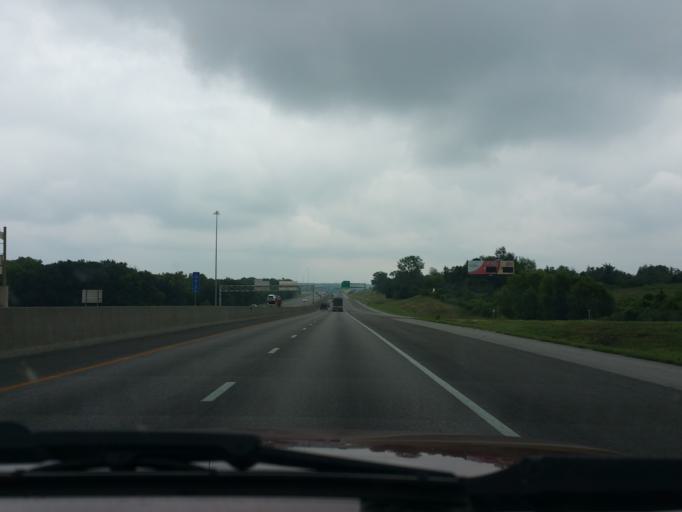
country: US
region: Kansas
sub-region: Wyandotte County
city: Edwardsville
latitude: 39.1060
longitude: -94.8334
